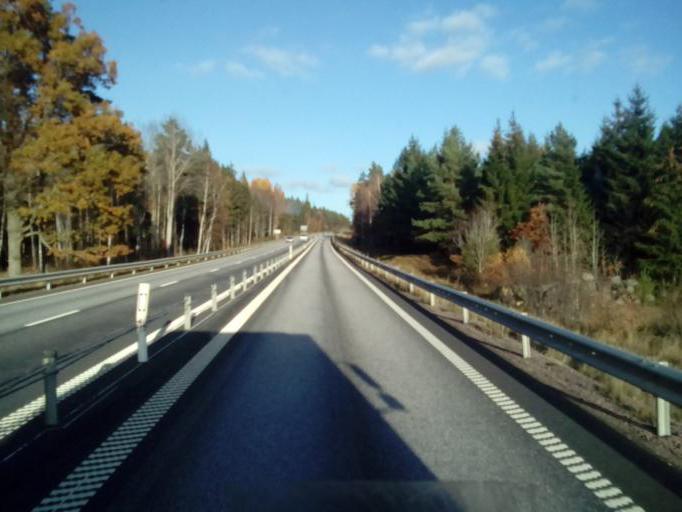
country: SE
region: Kalmar
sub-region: Vimmerby Kommun
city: Vimmerby
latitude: 57.7116
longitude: 16.0482
